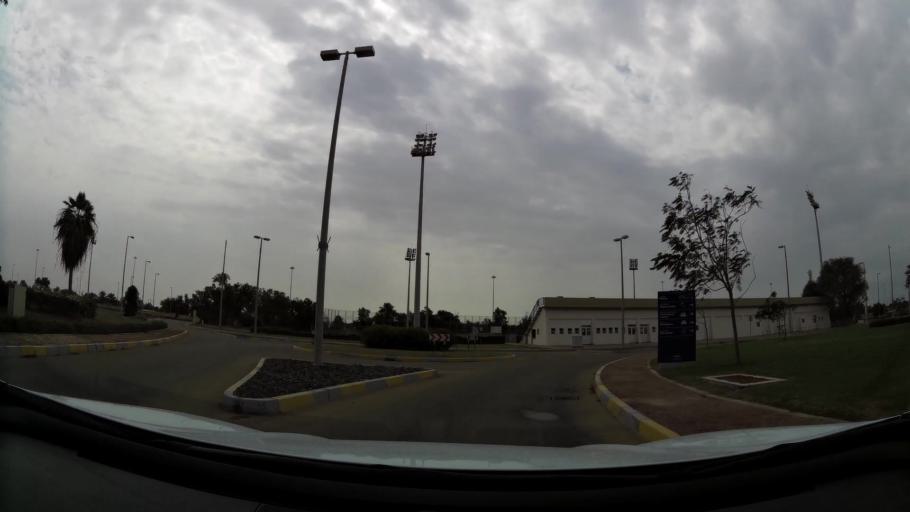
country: AE
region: Abu Dhabi
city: Abu Dhabi
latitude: 24.4126
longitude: 54.4605
